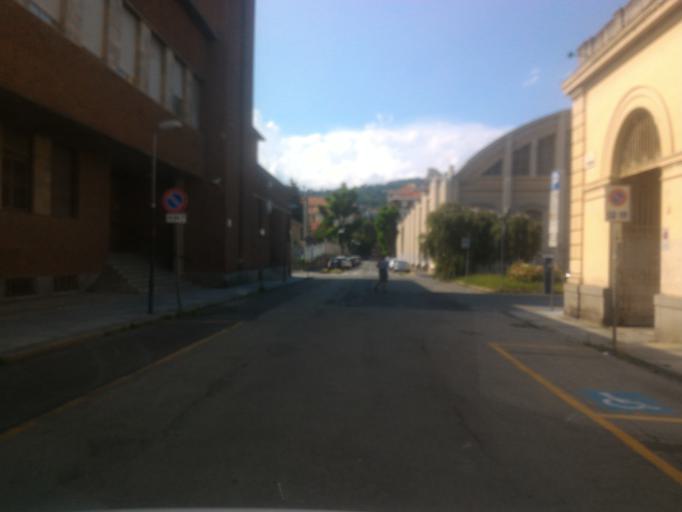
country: IT
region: Piedmont
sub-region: Provincia di Torino
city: Pinerolo
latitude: 44.8878
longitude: 7.3343
